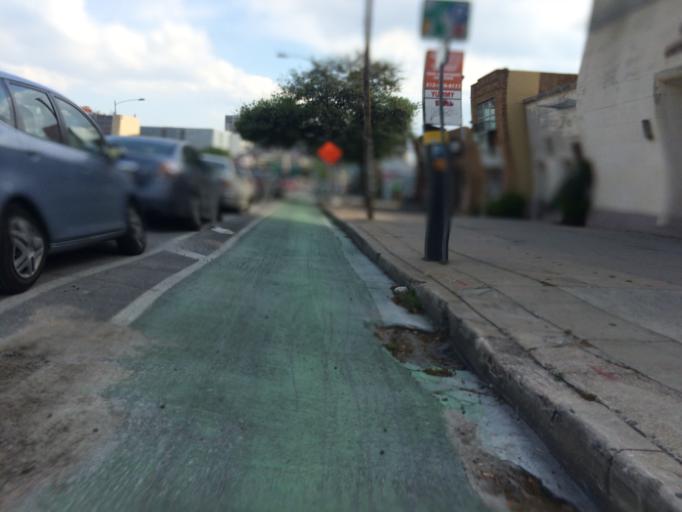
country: US
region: Texas
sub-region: Travis County
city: Austin
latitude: 30.2833
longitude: -97.7421
